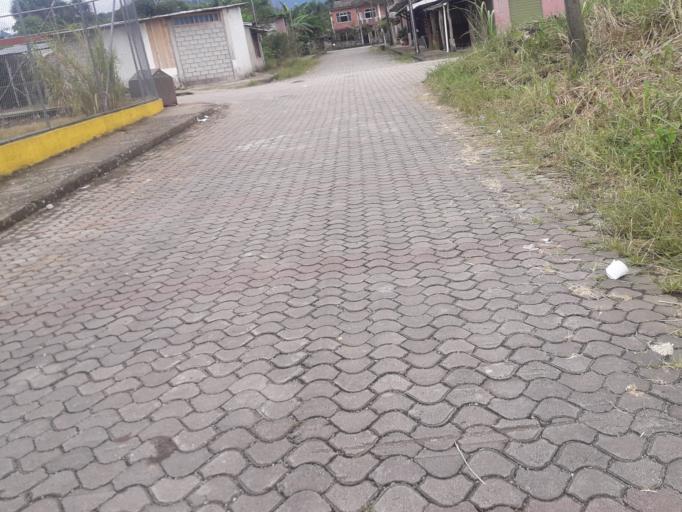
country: EC
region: Napo
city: Tena
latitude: -0.9859
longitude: -77.8292
